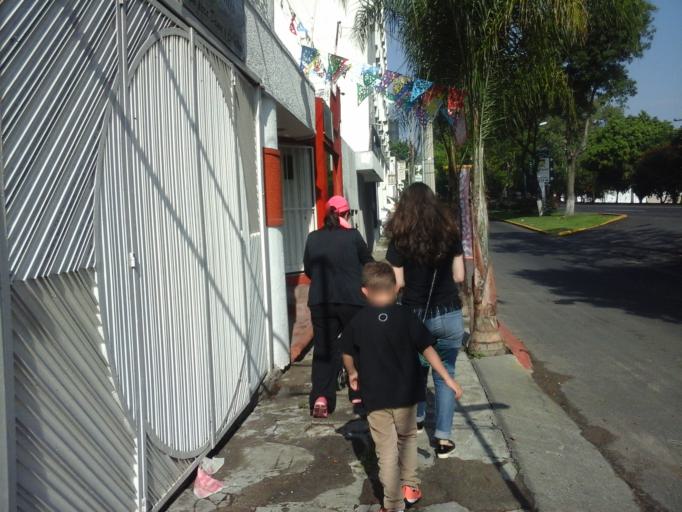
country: MX
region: Michoacan
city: Morelia
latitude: 19.6810
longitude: -101.1845
